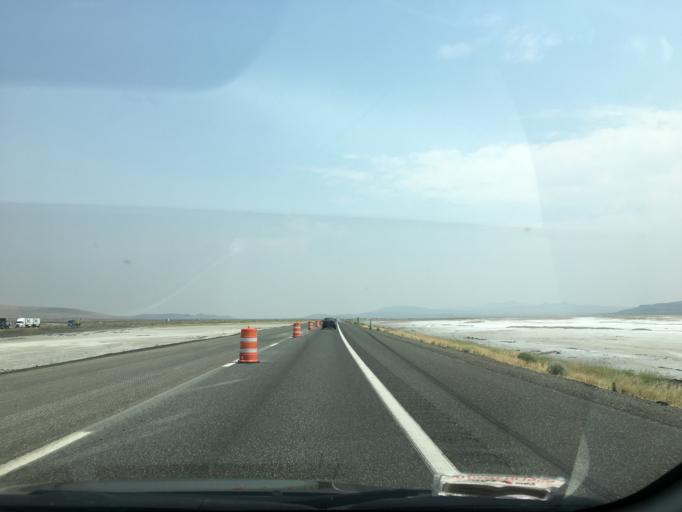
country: US
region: Nevada
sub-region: Lyon County
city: Fernley
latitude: 39.7058
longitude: -119.0963
